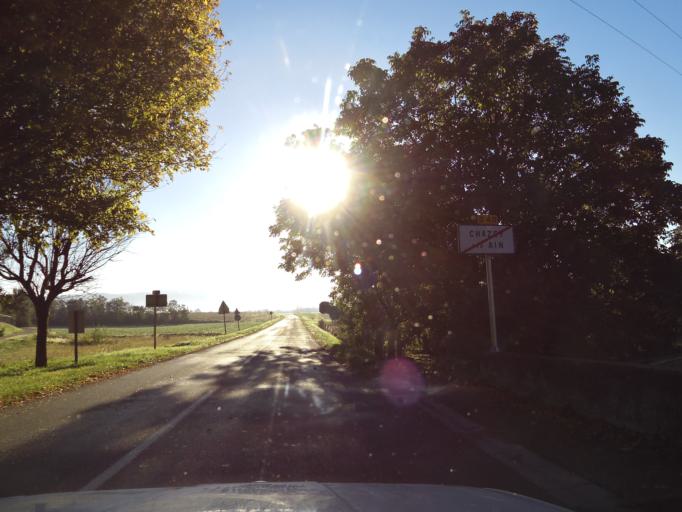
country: FR
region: Rhone-Alpes
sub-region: Departement de l'Ain
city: Chazey-sur-Ain
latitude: 45.8919
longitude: 5.2581
